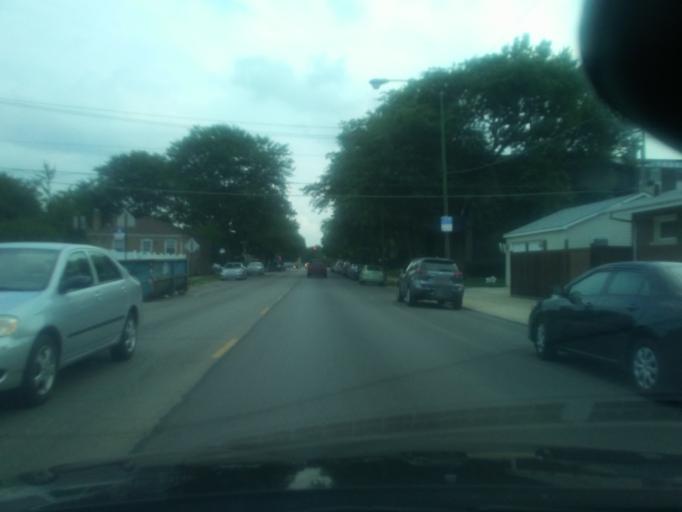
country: US
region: Illinois
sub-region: Cook County
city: Lincolnwood
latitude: 42.0066
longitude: -87.6998
